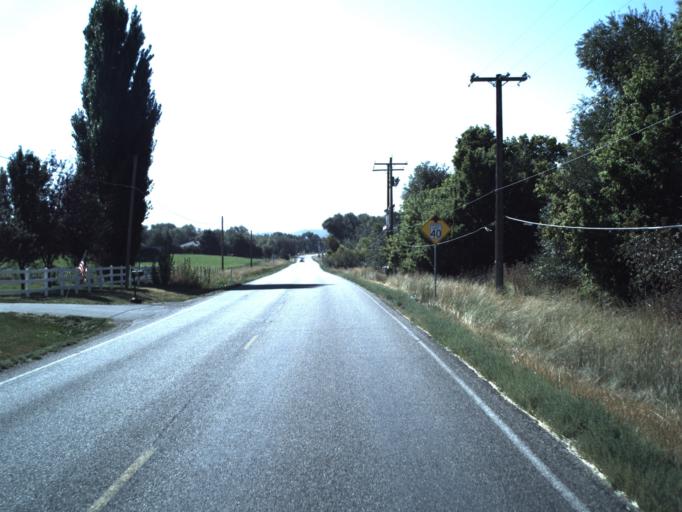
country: US
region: Utah
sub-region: Cache County
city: Hyrum
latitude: 41.5794
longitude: -111.8387
